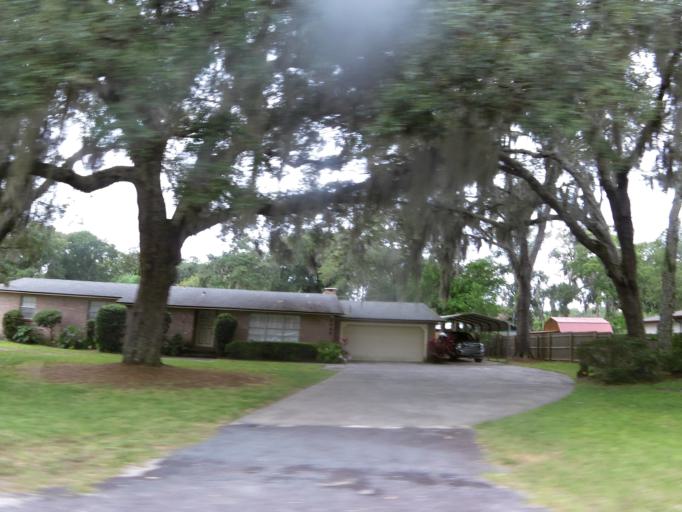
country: US
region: Florida
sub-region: Clay County
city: Bellair-Meadowbrook Terrace
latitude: 30.2542
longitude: -81.7308
